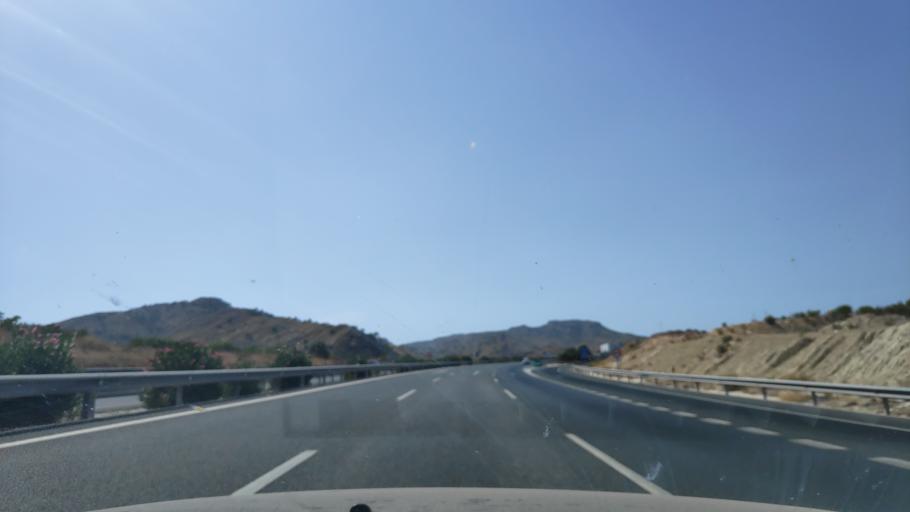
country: ES
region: Murcia
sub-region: Murcia
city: Archena
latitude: 38.1544
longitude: -1.2932
